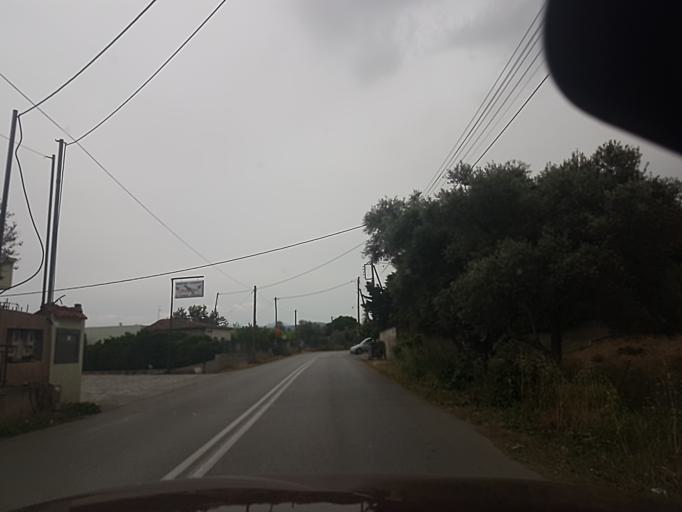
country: GR
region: Central Greece
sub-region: Nomos Evvoias
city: Mytikas
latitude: 38.4649
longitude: 23.6315
